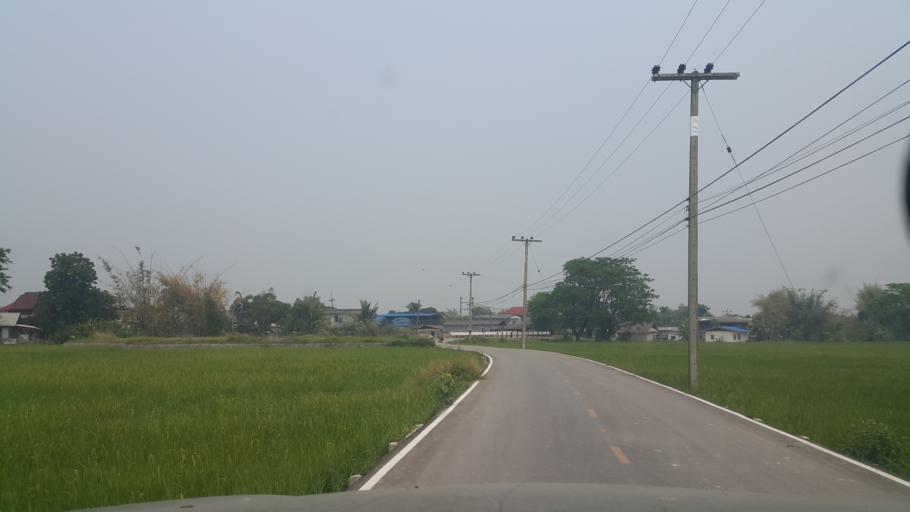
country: TH
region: Lampang
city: Hang Chat
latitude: 18.2722
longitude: 99.2524
